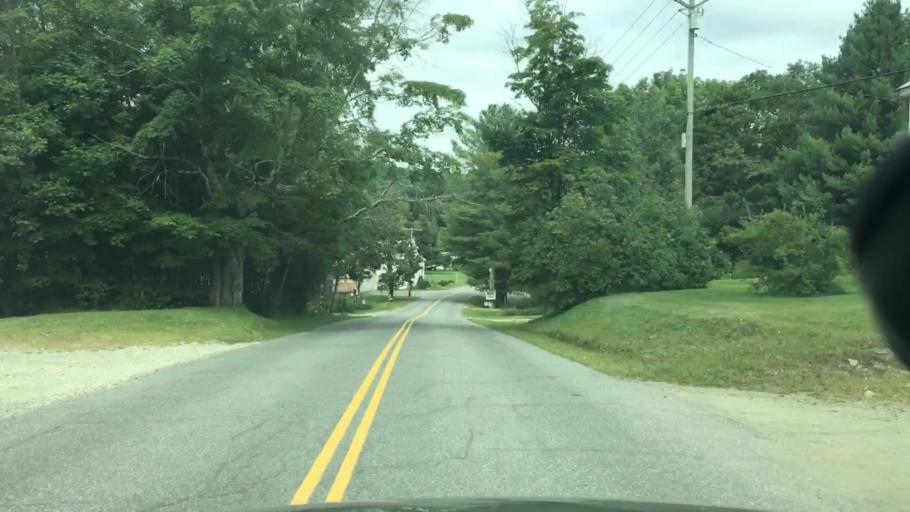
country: US
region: Massachusetts
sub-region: Franklin County
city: Colrain
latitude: 42.7851
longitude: -72.7688
